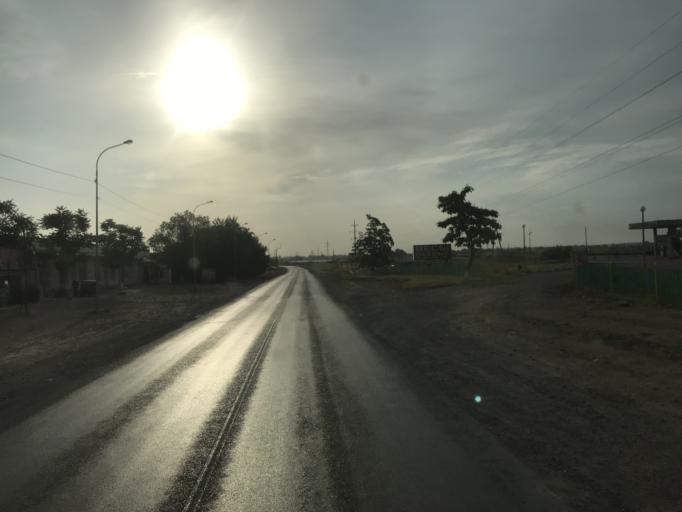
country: KZ
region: Ongtustik Qazaqstan
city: Saryaghash
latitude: 41.4913
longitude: 69.2856
